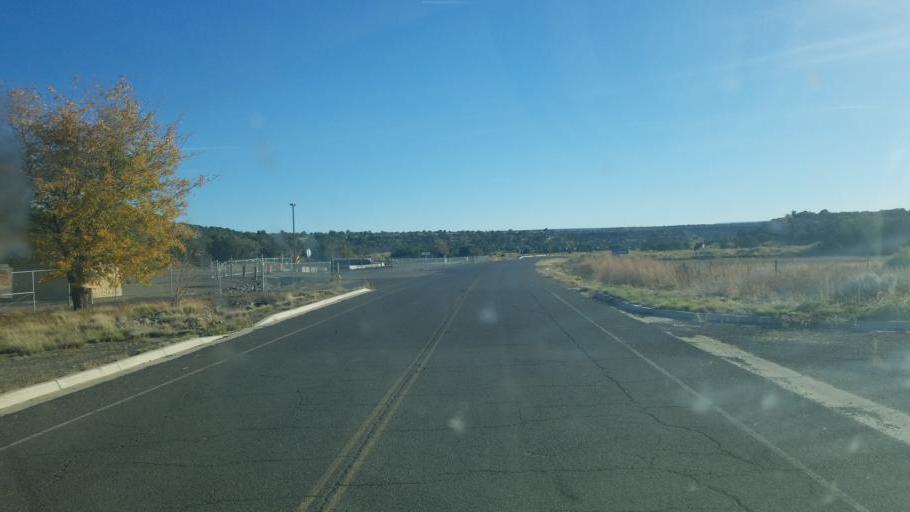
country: US
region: New Mexico
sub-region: Cibola County
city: Skyline-Ganipa
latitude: 35.0736
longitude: -107.5562
